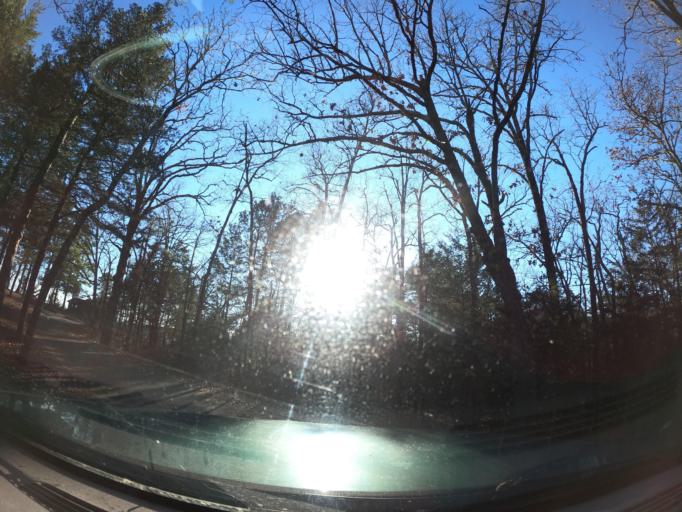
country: US
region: Oklahoma
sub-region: Latimer County
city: Wilburton
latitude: 34.9760
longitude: -95.3561
